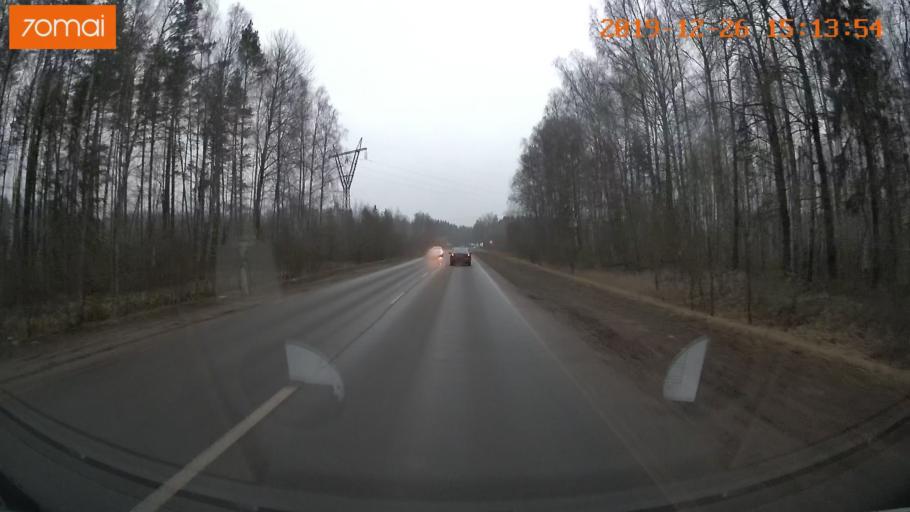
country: RU
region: Jaroslavl
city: Rybinsk
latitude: 58.1113
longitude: 38.8824
